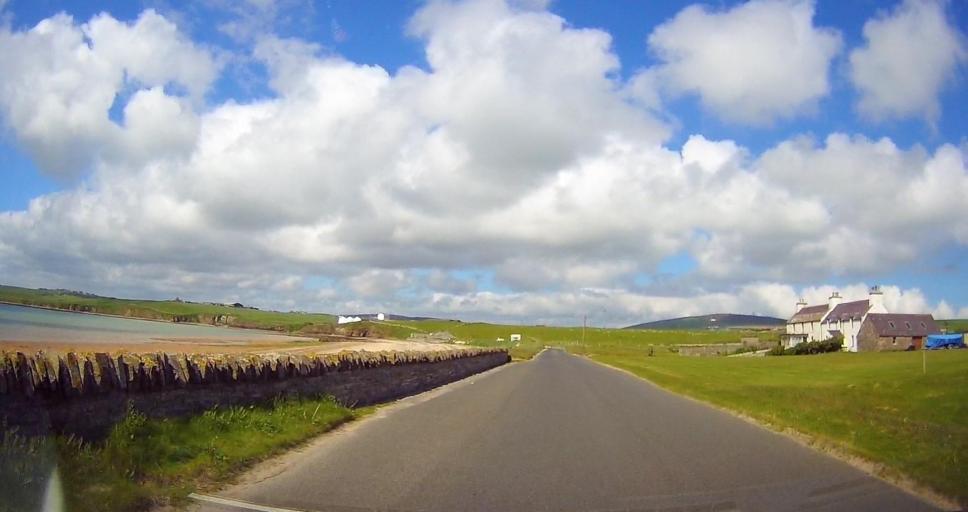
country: GB
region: Scotland
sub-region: Orkney Islands
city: Orkney
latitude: 58.9617
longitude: -2.9729
